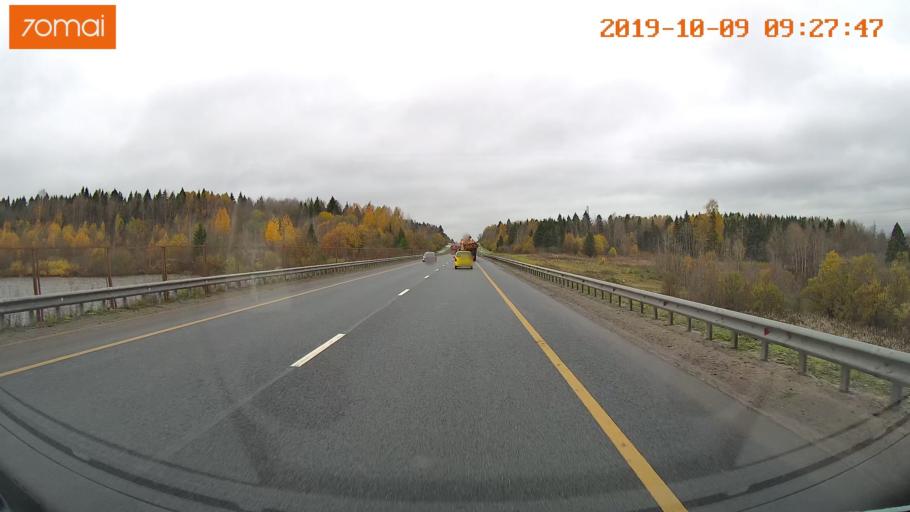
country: RU
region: Vologda
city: Vologda
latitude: 59.1166
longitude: 39.9746
